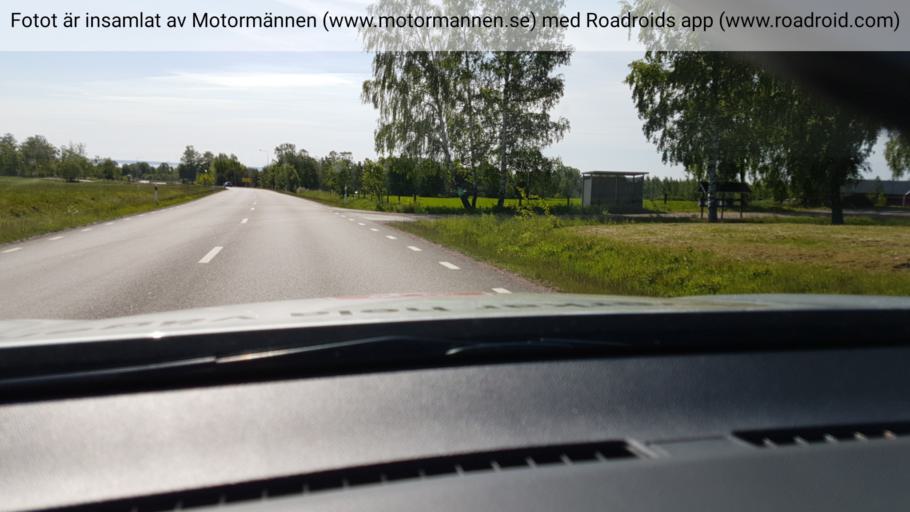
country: SE
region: Vaestra Goetaland
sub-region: Hjo Kommun
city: Hjo
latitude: 58.3238
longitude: 14.2627
